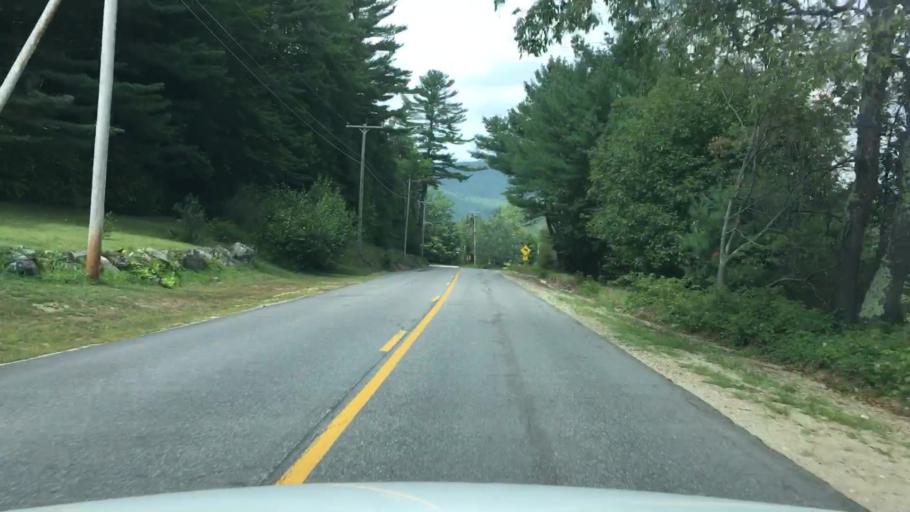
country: US
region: Maine
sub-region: Oxford County
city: Rumford
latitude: 44.5328
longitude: -70.6427
